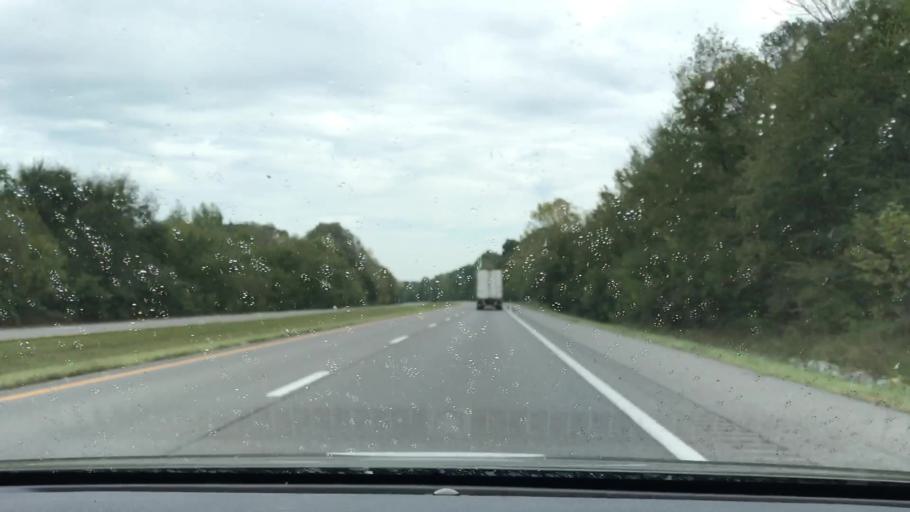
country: US
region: Kentucky
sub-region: Graves County
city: Mayfield
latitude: 36.7981
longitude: -88.5055
